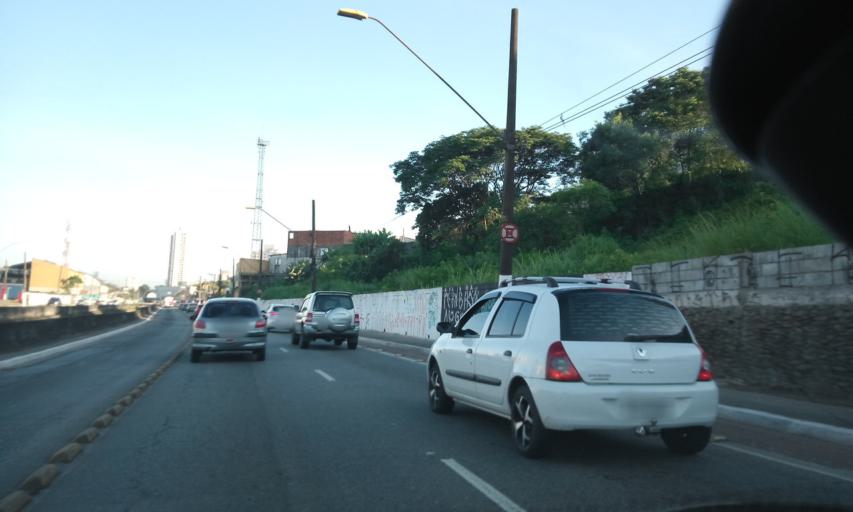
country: BR
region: Sao Paulo
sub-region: Santo Andre
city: Santo Andre
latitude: -23.6797
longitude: -46.5053
